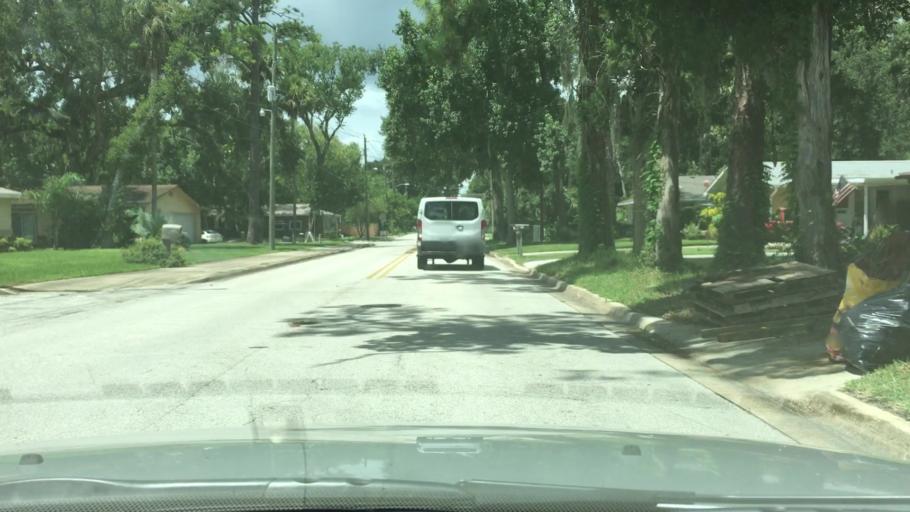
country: US
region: Florida
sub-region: Volusia County
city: Ormond Beach
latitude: 29.2720
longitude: -81.0654
